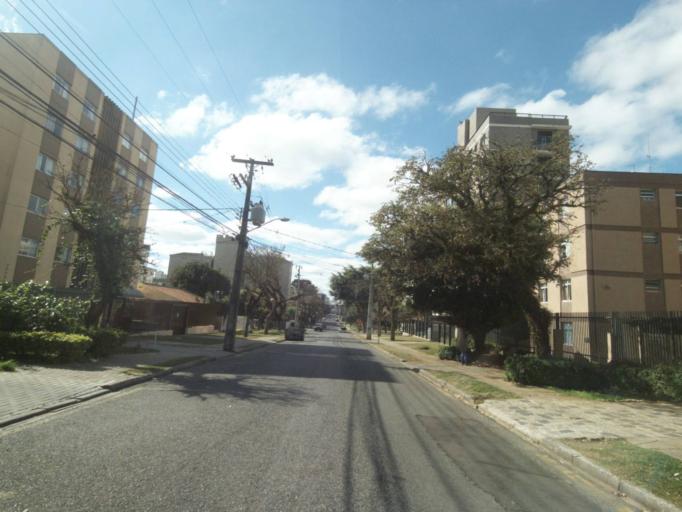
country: BR
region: Parana
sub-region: Curitiba
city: Curitiba
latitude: -25.4655
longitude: -49.2860
